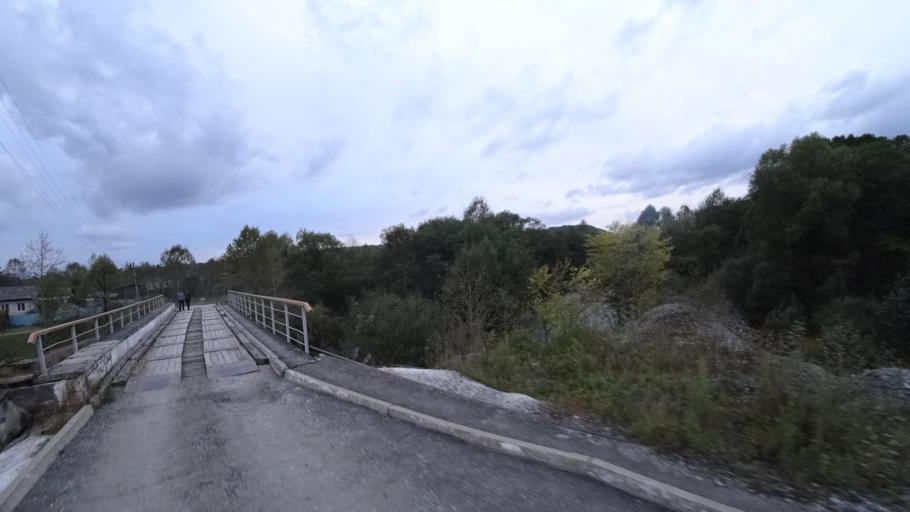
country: RU
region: Jewish Autonomous Oblast
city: Izvestkovyy
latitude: 48.9909
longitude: 131.5554
